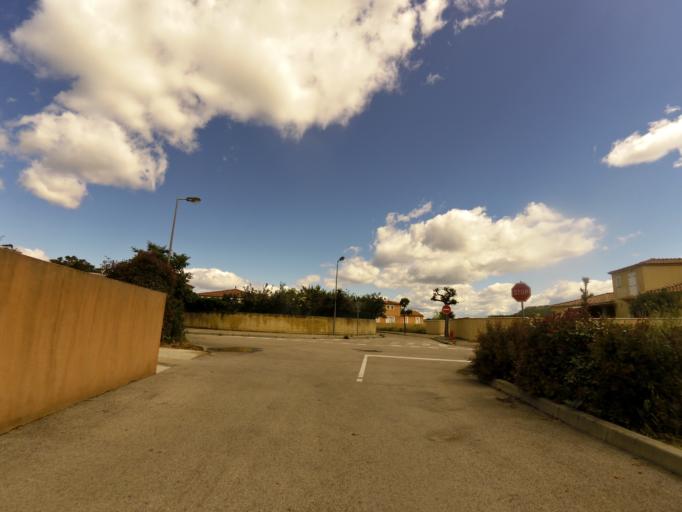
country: FR
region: Languedoc-Roussillon
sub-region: Departement du Gard
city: Calvisson
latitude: 43.7799
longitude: 4.2077
